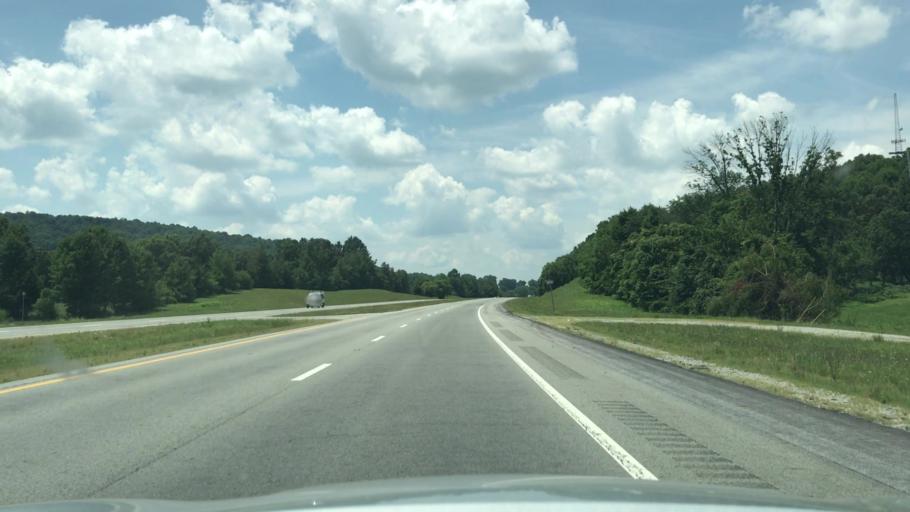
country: US
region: Tennessee
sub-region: Putnam County
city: Algood
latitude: 36.2156
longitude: -85.4187
